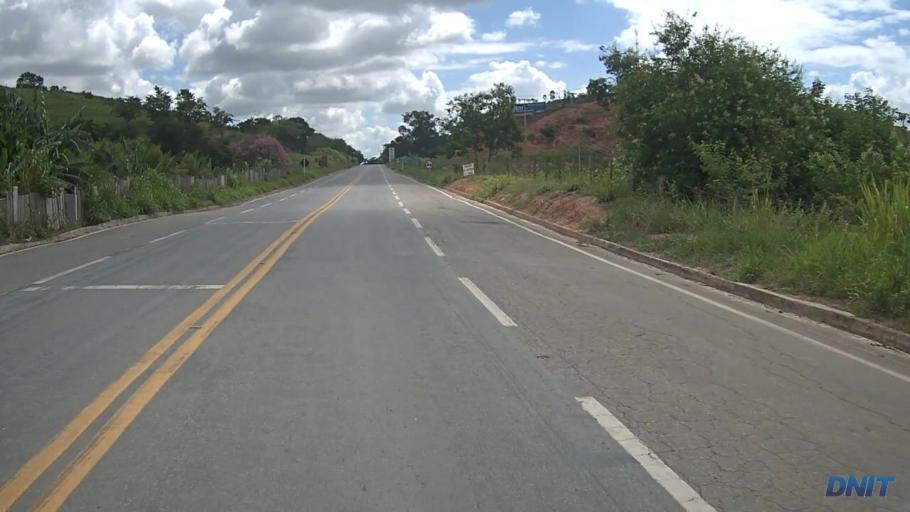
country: BR
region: Minas Gerais
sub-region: Governador Valadares
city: Governador Valadares
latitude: -18.9556
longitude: -42.0755
